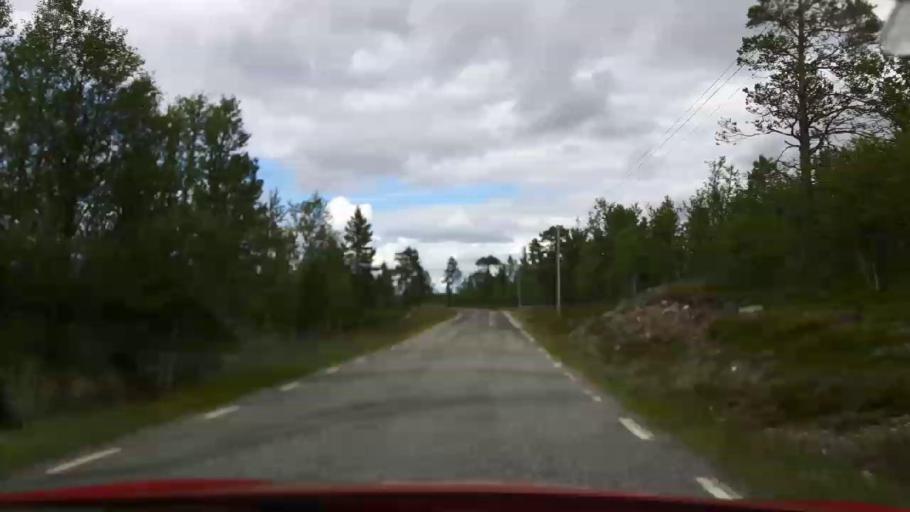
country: NO
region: Hedmark
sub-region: Engerdal
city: Engerdal
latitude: 62.3391
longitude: 12.7995
